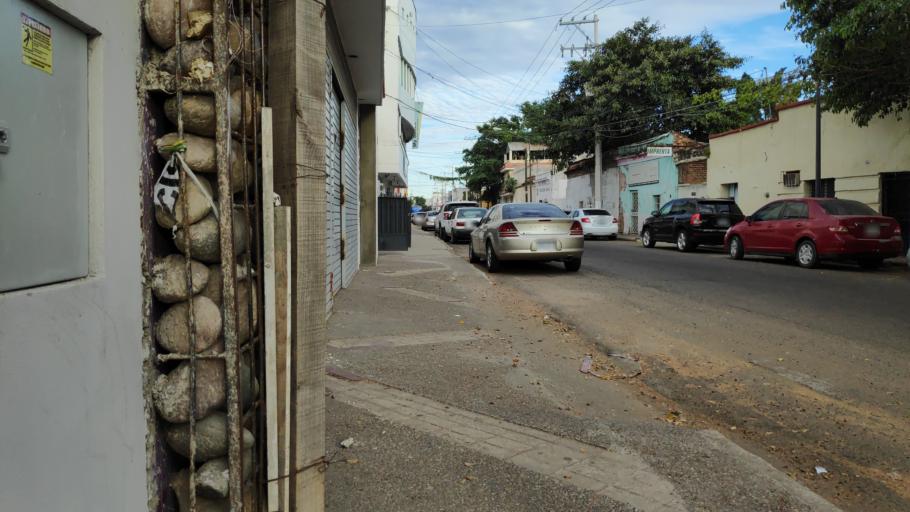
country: MX
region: Sinaloa
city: Culiacan
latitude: 24.8111
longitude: -107.4000
